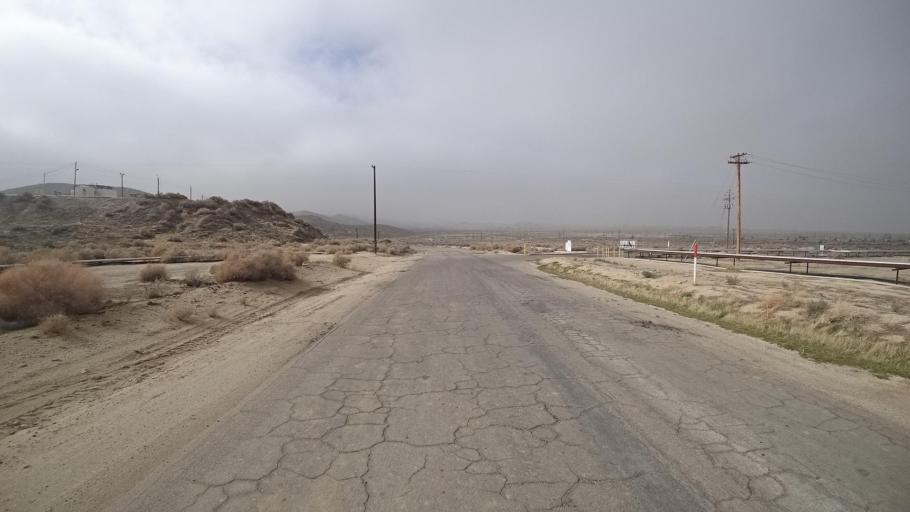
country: US
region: California
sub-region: Kern County
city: Maricopa
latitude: 35.0385
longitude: -119.3755
